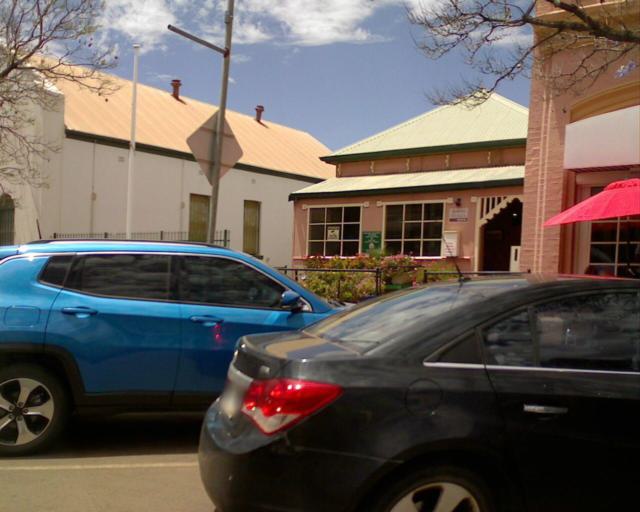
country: AU
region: Western Australia
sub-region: Kalgoorlie/Boulder
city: Boulder
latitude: -30.7819
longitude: 121.4872
